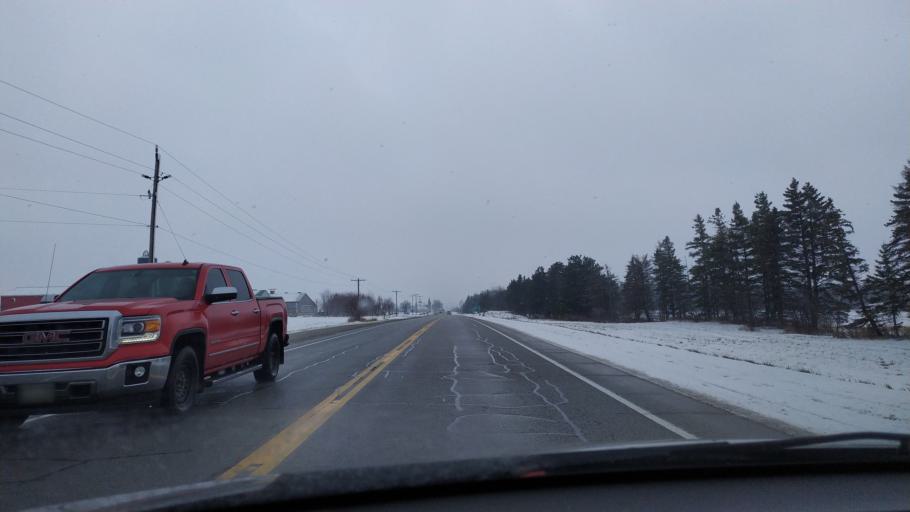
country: CA
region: Ontario
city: Waterloo
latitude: 43.6271
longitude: -80.7030
